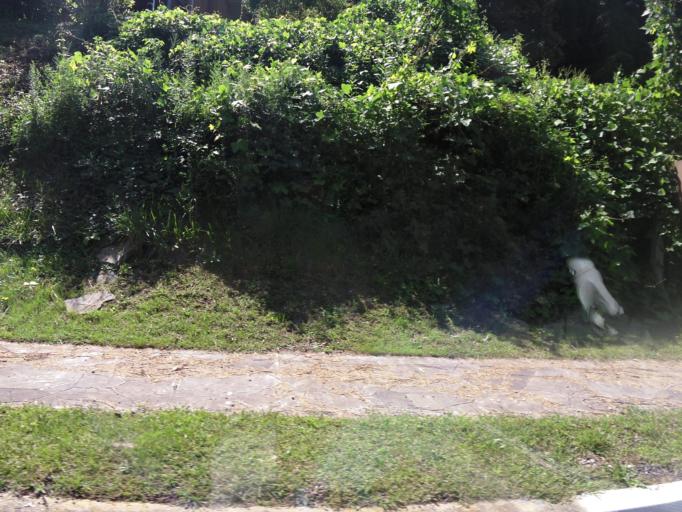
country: US
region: Kentucky
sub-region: Leslie County
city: Hyden
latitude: 37.1623
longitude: -83.3758
